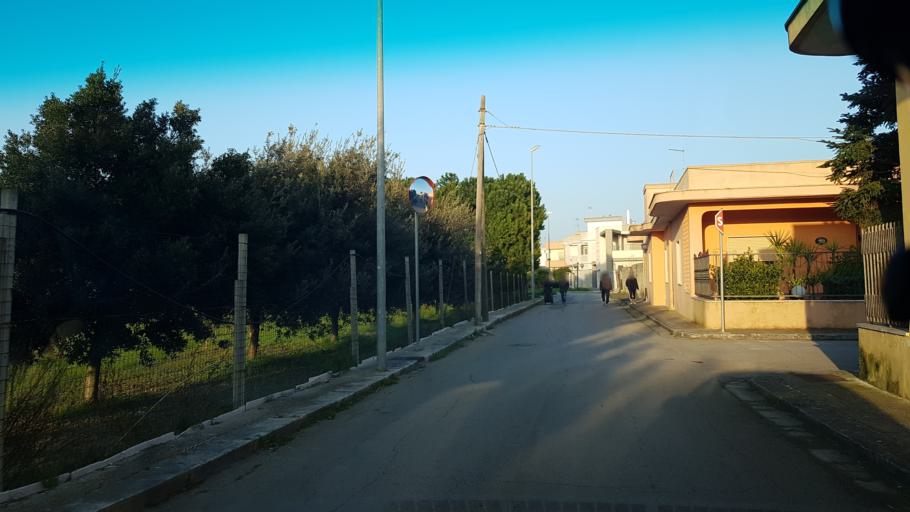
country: IT
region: Apulia
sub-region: Provincia di Brindisi
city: Mesagne
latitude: 40.5557
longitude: 17.7980
